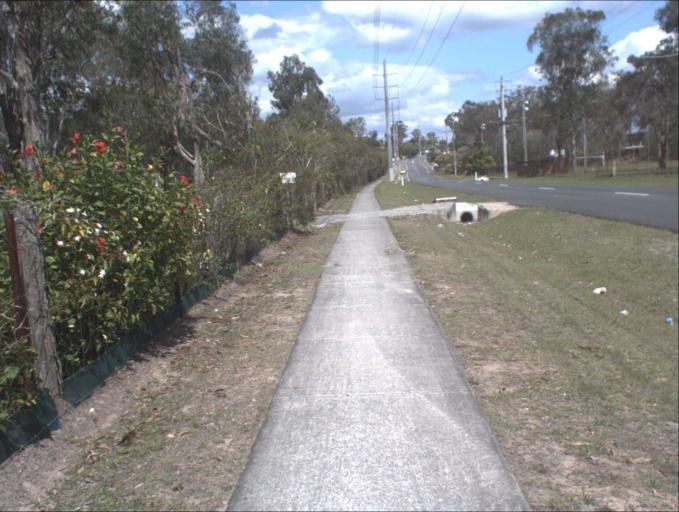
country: AU
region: Queensland
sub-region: Logan
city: Logan City
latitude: -27.6662
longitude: 153.0901
